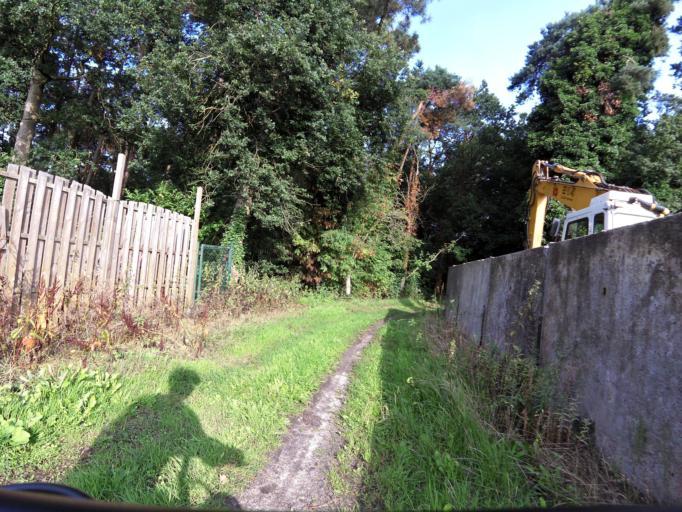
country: NL
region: North Brabant
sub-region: Gemeente Woensdrecht
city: Woensdrecht
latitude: 51.4386
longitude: 4.3752
